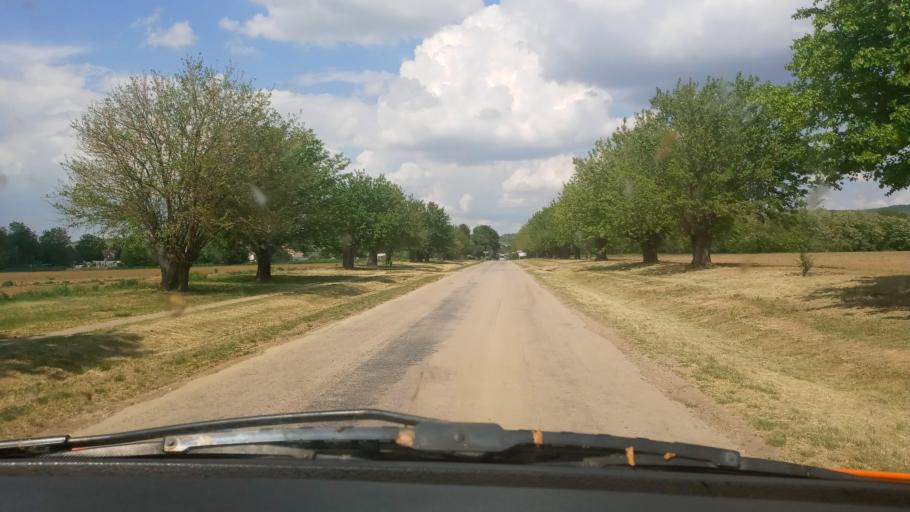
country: HU
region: Baranya
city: Siklos
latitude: 45.8525
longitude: 18.3594
